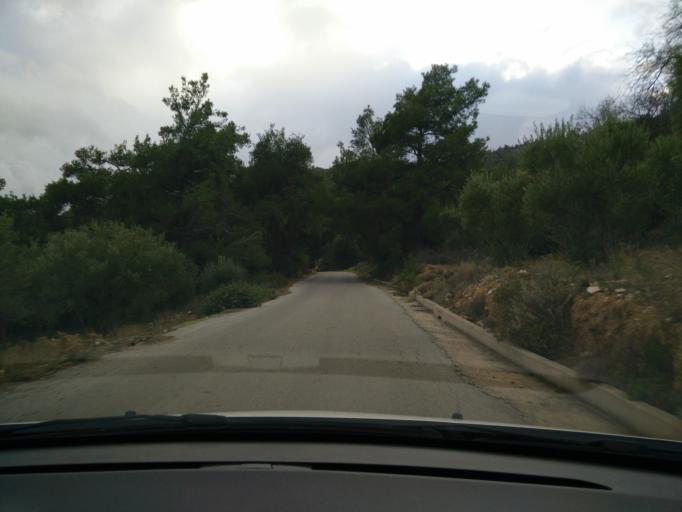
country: GR
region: Crete
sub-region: Nomos Lasithiou
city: Kritsa
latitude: 35.1020
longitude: 25.6931
